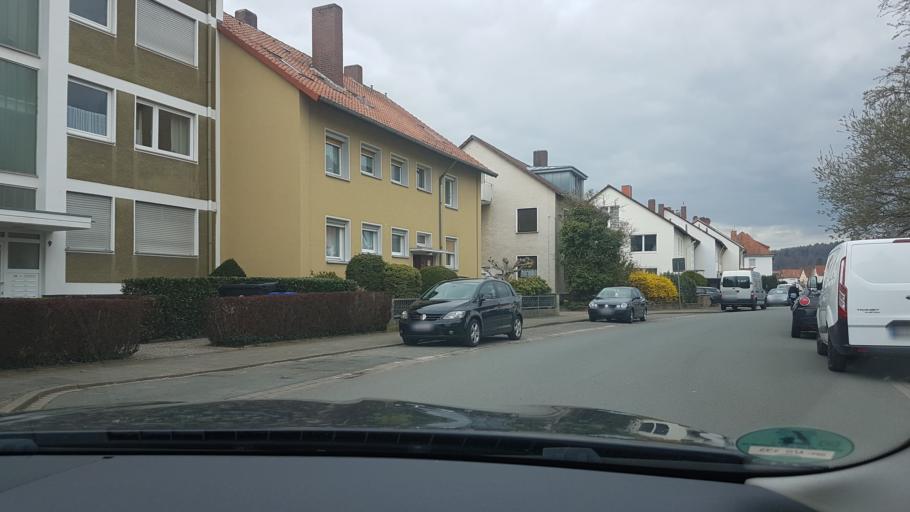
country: DE
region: Lower Saxony
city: Hameln
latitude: 52.1166
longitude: 9.3544
